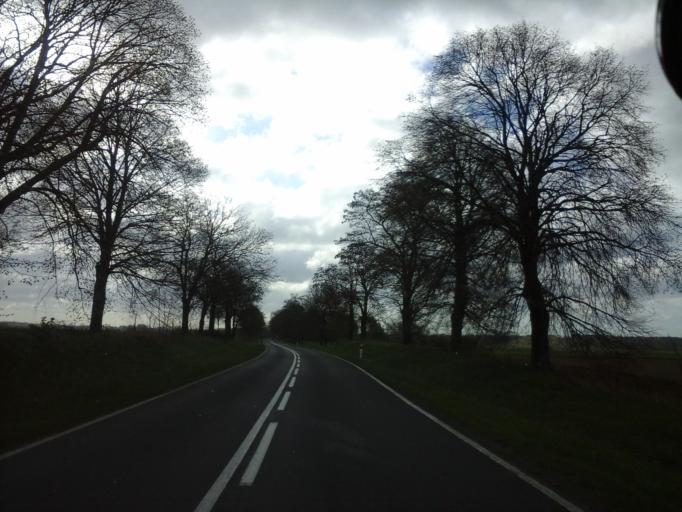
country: PL
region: West Pomeranian Voivodeship
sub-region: Powiat choszczenski
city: Krzecin
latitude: 53.1370
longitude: 15.5217
